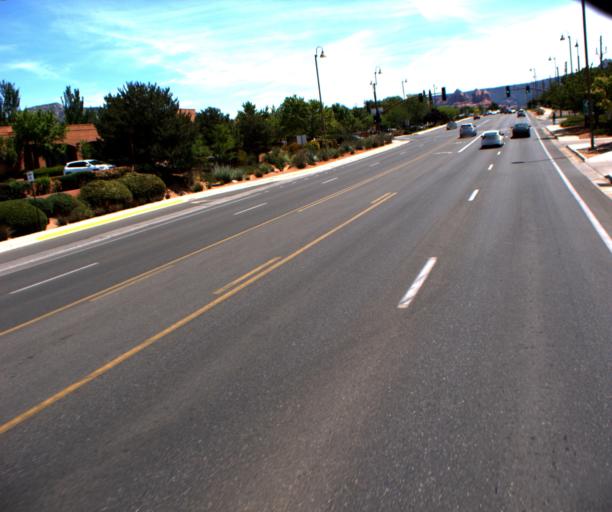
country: US
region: Arizona
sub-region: Yavapai County
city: West Sedona
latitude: 34.8632
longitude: -111.8010
